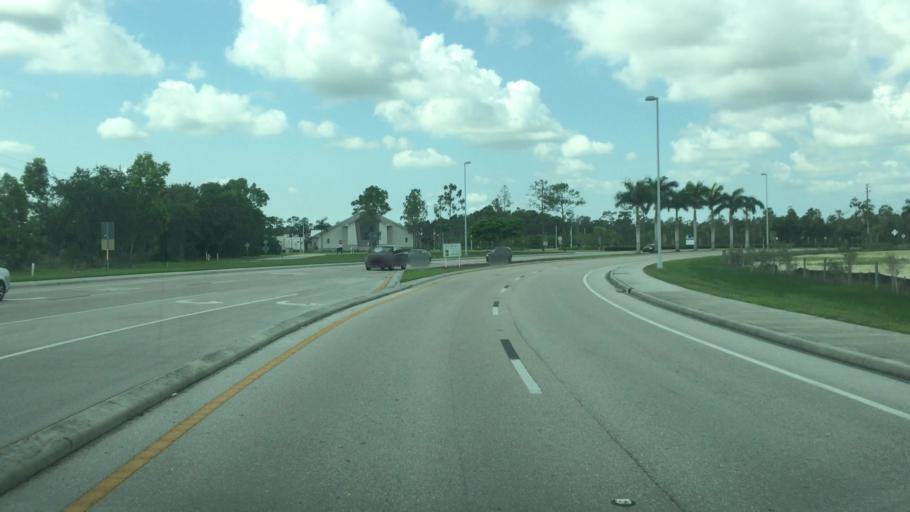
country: US
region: Florida
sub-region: Lee County
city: Fort Myers
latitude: 26.5967
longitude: -81.8411
